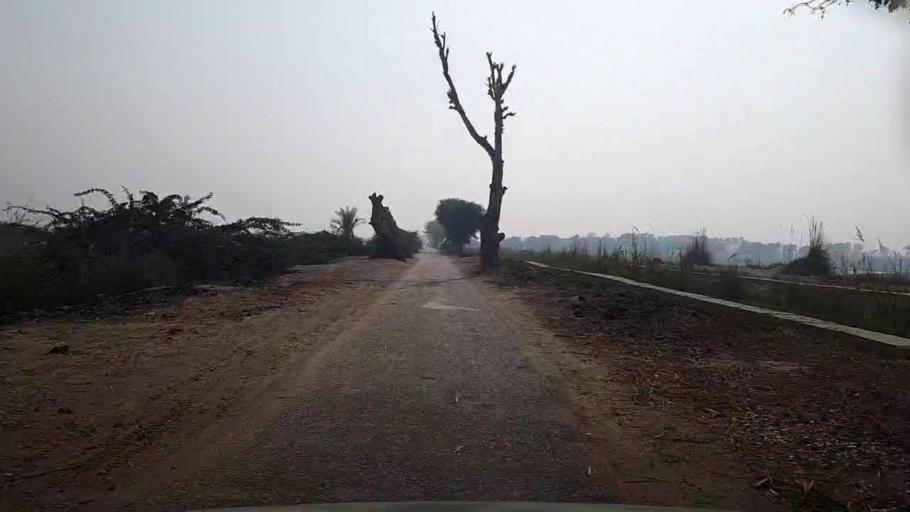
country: PK
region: Sindh
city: Setharja Old
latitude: 27.1072
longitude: 68.5082
